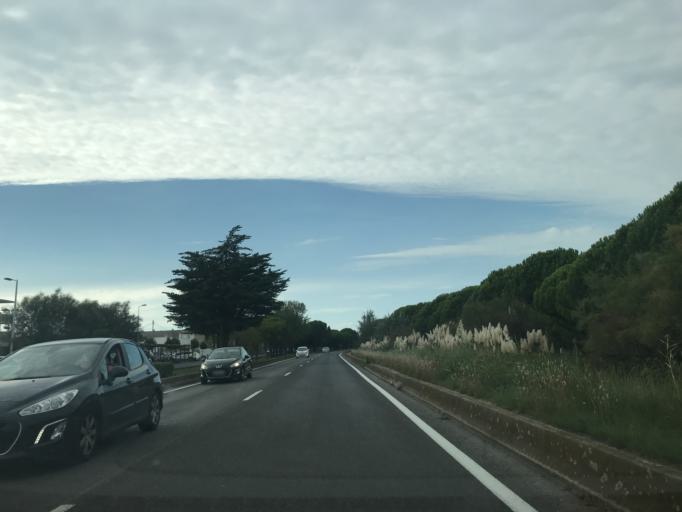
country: FR
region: Languedoc-Roussillon
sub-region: Departement du Gard
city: Le Grau-du-Roi
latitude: 43.5529
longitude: 4.1126
